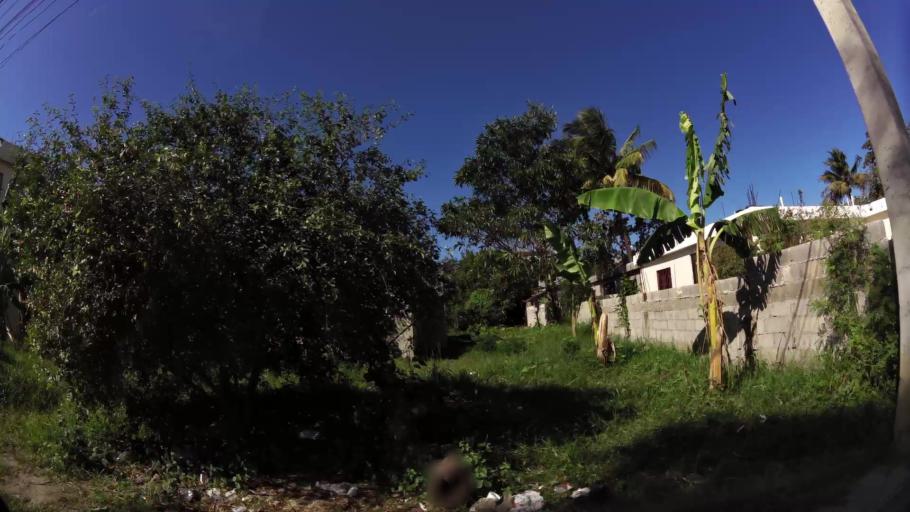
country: DO
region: San Cristobal
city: San Cristobal
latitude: 18.4335
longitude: -70.1230
